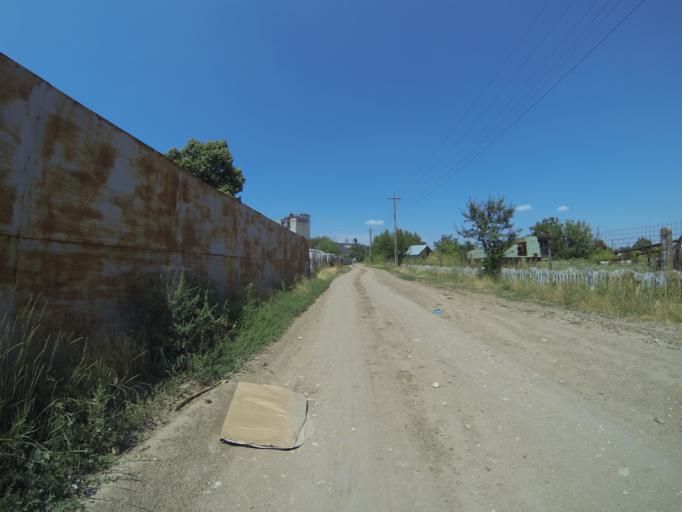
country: RO
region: Dolj
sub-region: Comuna Segarcea
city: Segarcea
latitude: 44.0890
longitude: 23.7320
